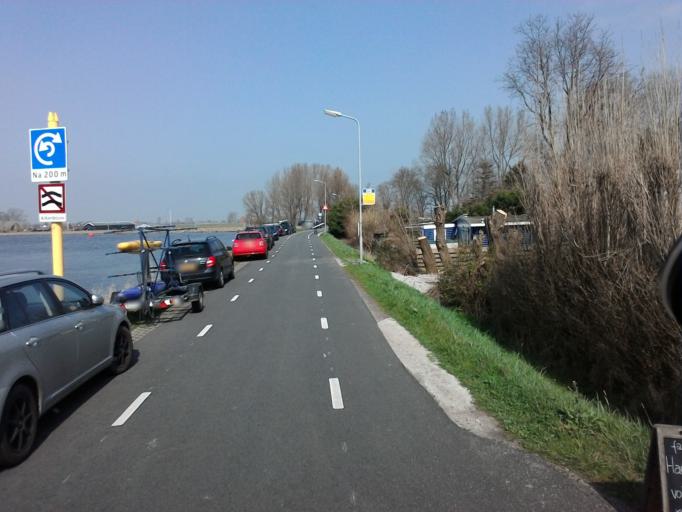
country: NL
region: North Holland
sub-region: Gemeente Zaanstad
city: Zaanstad
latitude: 52.5056
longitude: 4.7943
